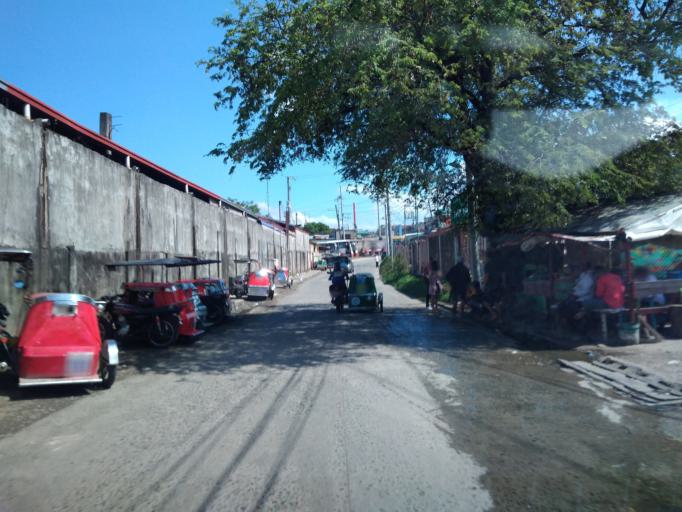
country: PH
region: Central Luzon
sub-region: Province of Bulacan
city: Bitungol
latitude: 14.8582
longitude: 121.0476
